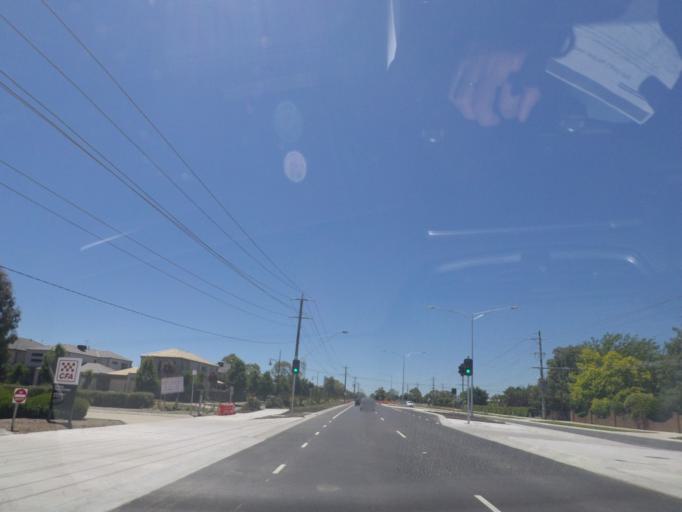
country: AU
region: Victoria
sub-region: Whittlesea
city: Epping
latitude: -37.6371
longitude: 145.0265
